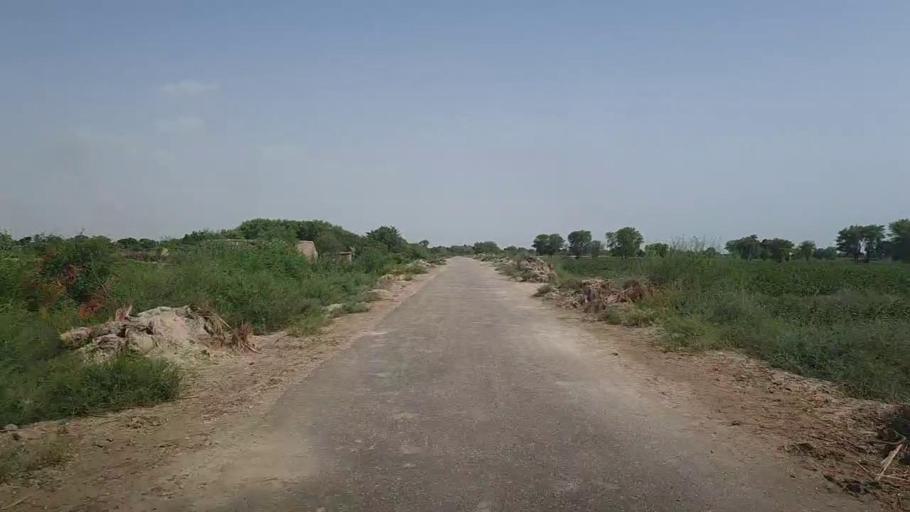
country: PK
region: Sindh
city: Pad Idan
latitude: 26.8101
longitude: 68.3300
